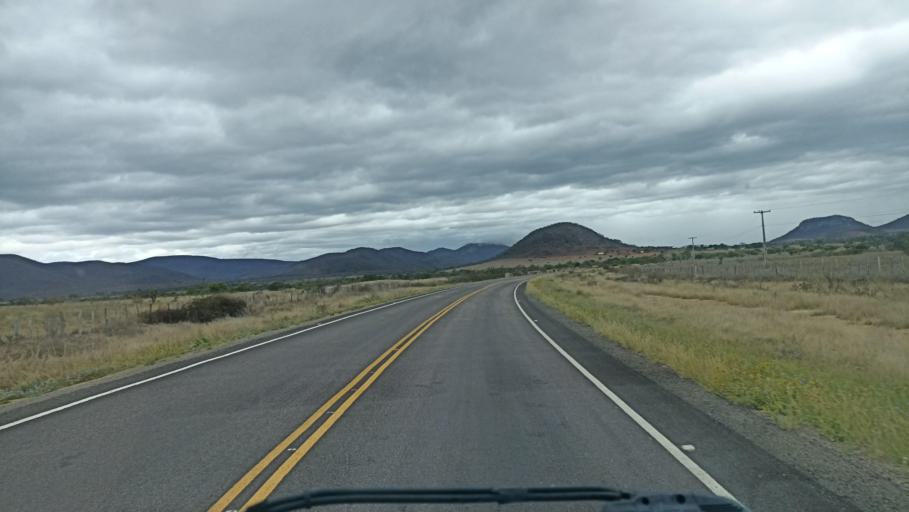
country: BR
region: Bahia
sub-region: Iacu
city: Iacu
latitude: -12.9225
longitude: -40.4159
